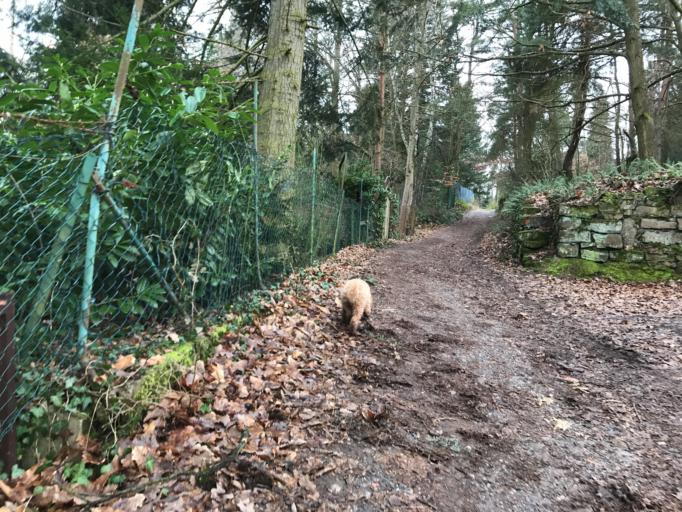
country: DE
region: Rheinland-Pfalz
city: Wachenheim
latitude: 49.4336
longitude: 8.1699
